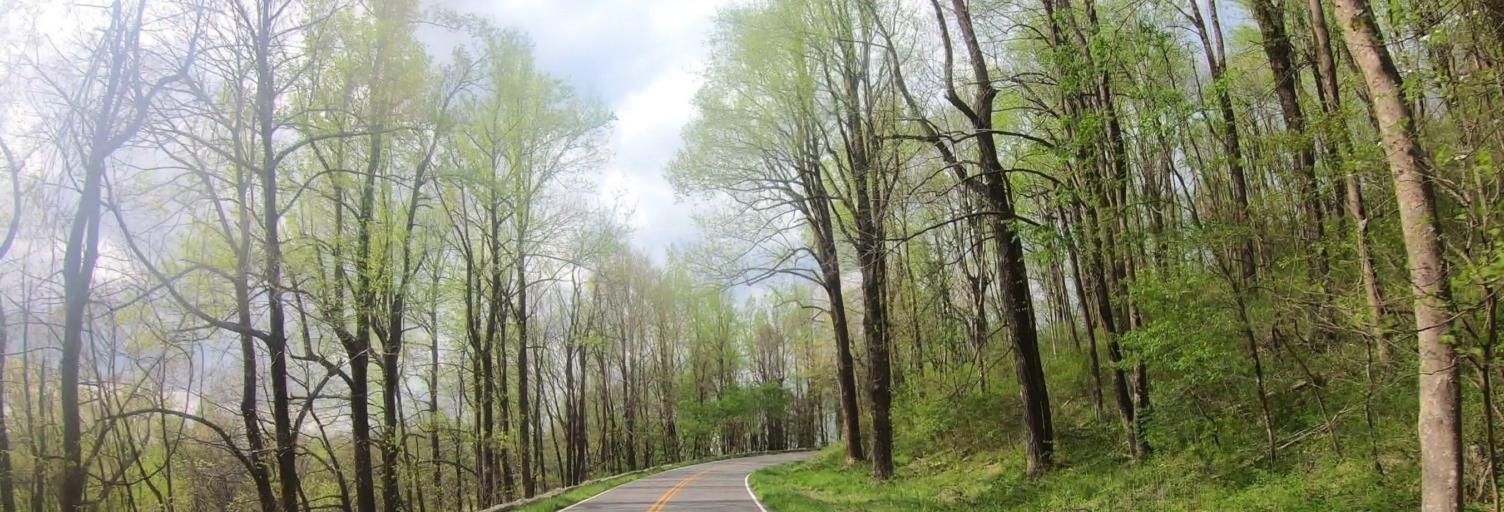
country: US
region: Virginia
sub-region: Rockingham County
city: Elkton
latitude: 38.3039
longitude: -78.6227
